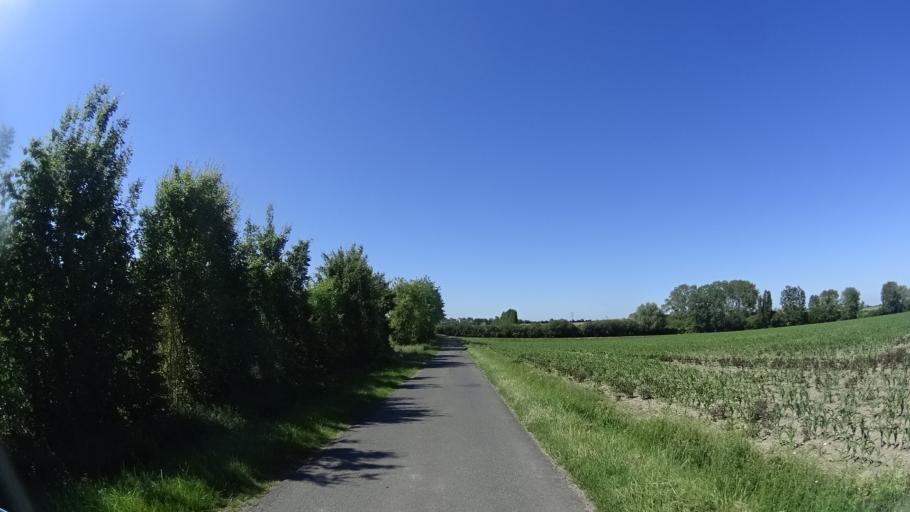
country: FR
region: Pays de la Loire
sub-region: Departement de Maine-et-Loire
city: Doue-la-Fontaine
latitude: 47.2443
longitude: -0.2910
